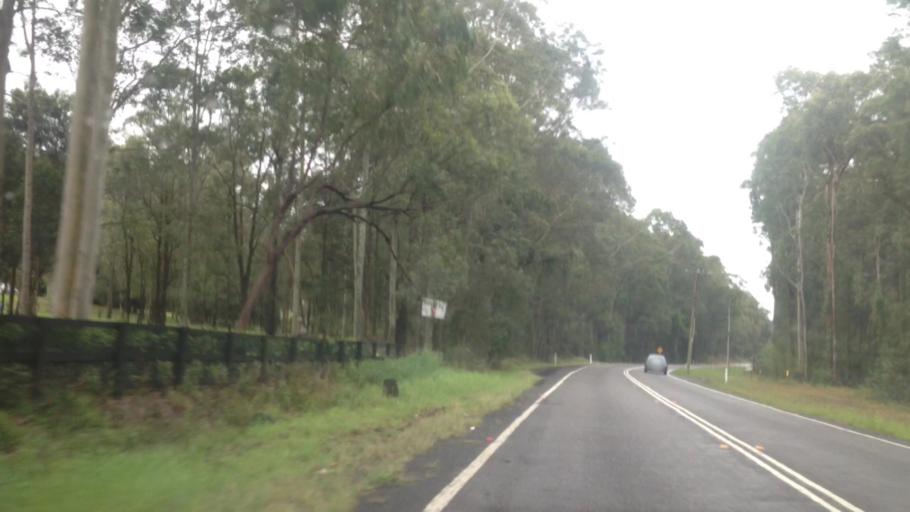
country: AU
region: New South Wales
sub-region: Wyong Shire
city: Little Jilliby
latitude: -33.2538
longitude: 151.3972
